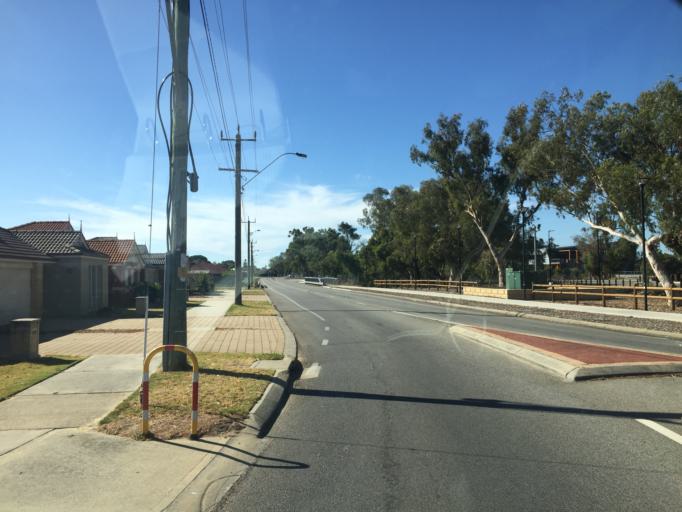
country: AU
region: Western Australia
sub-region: Gosnells
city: Kenwick
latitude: -32.0259
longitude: 115.9681
